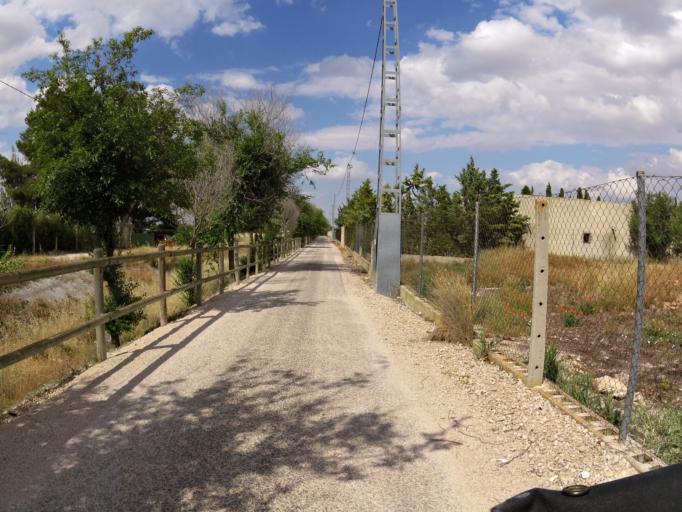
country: ES
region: Castille-La Mancha
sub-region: Provincia de Albacete
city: Albacete
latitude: 38.9739
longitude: -1.9284
